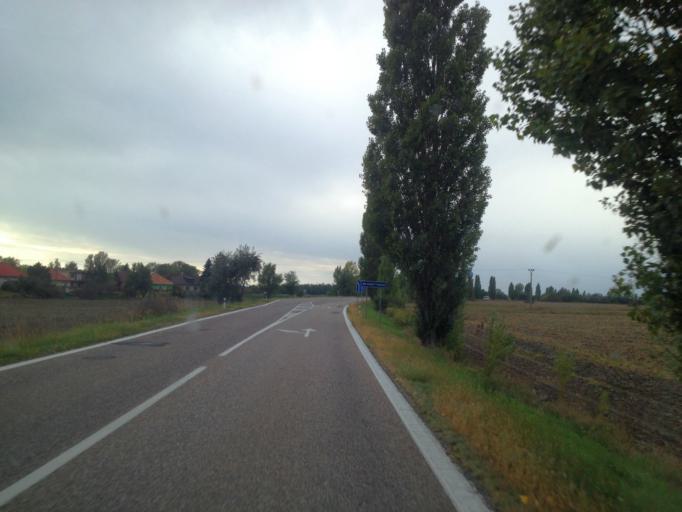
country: HU
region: Komarom-Esztergom
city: Labatlan
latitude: 47.7688
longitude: 18.4785
